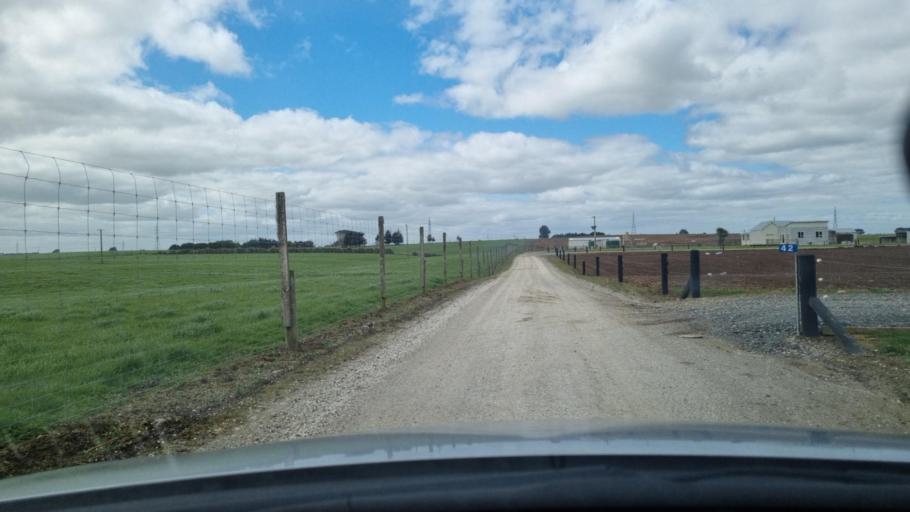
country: NZ
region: Southland
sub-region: Invercargill City
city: Invercargill
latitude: -46.4559
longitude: 168.4267
